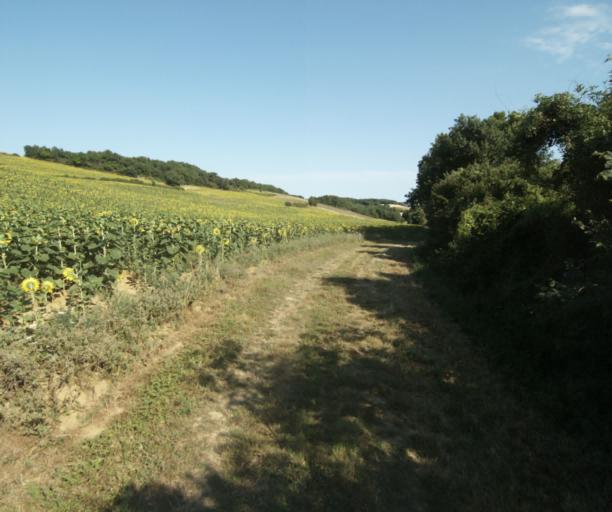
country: FR
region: Midi-Pyrenees
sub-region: Departement de la Haute-Garonne
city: Avignonet-Lauragais
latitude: 43.4152
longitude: 1.8114
